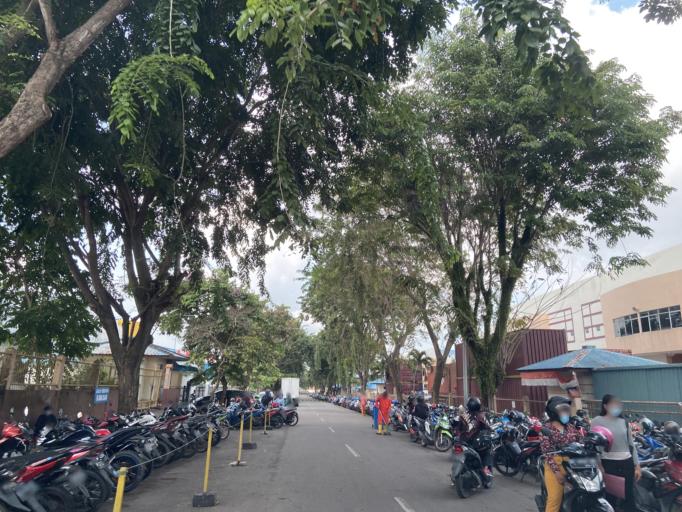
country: SG
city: Singapore
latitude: 1.1074
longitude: 104.0716
